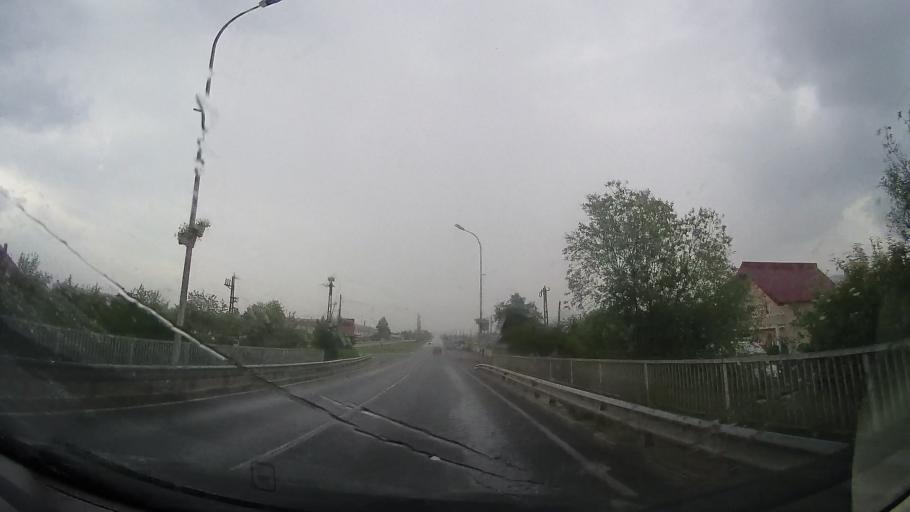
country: RO
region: Caras-Severin
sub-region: Comuna Buchin
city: Buchin
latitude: 45.3829
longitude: 22.2314
